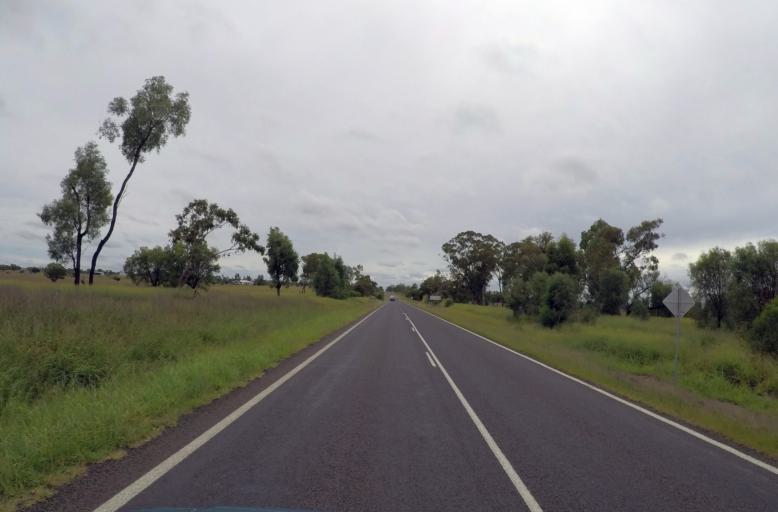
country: AU
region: Queensland
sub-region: Maranoa
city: Roma
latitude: -26.5158
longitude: 148.7854
